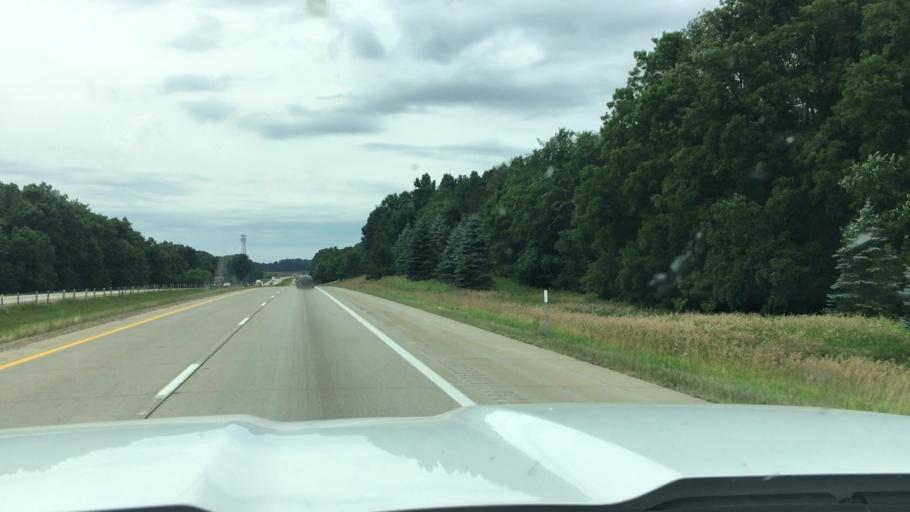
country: US
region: Michigan
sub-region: Allegan County
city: Otsego
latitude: 42.5049
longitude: -85.6540
